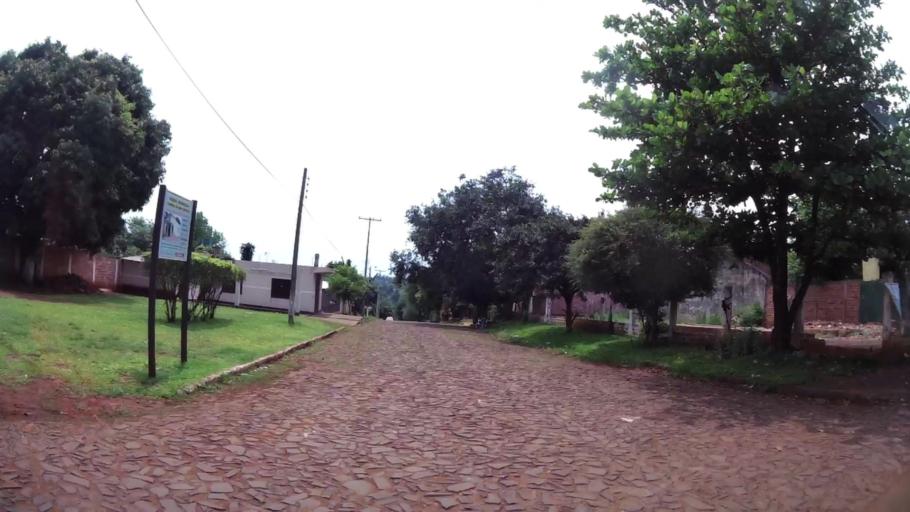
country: PY
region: Alto Parana
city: Ciudad del Este
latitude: -25.5020
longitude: -54.6221
